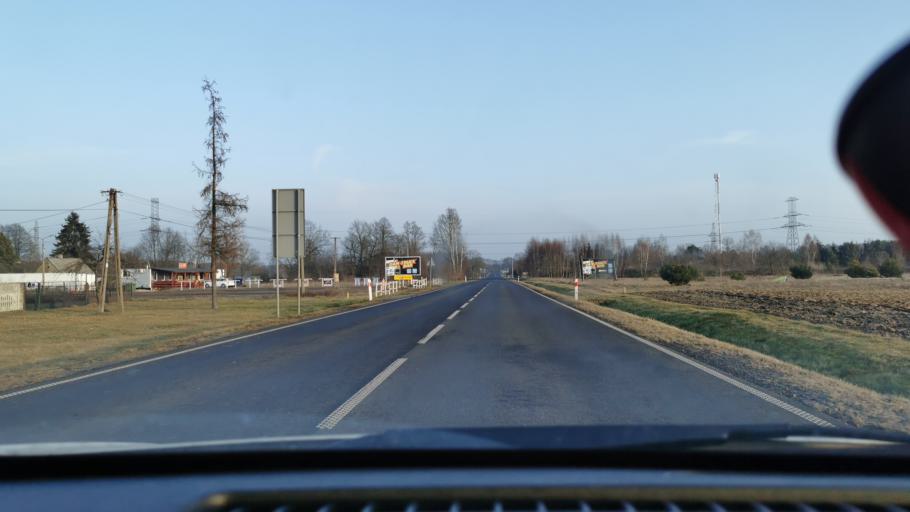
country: PL
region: Lodz Voivodeship
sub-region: Powiat belchatowski
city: Zelow
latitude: 51.5274
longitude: 19.2907
